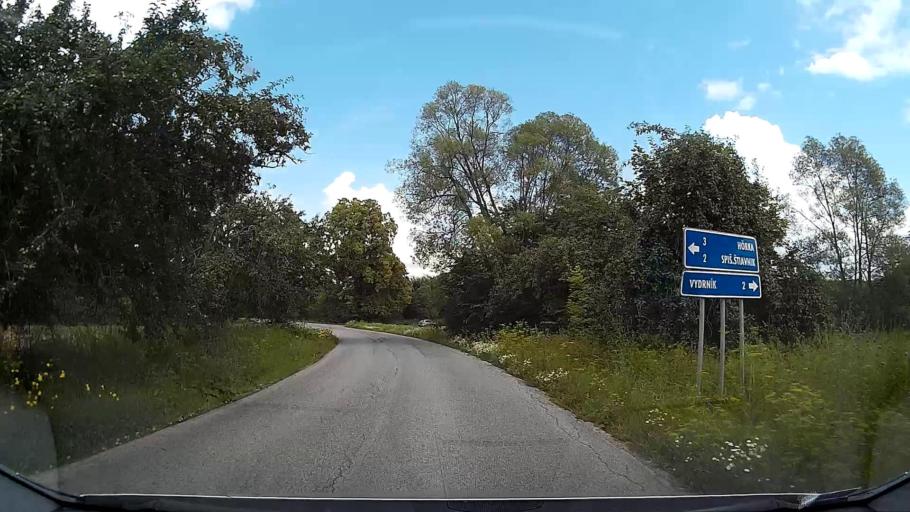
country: SK
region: Presovsky
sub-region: Okres Poprad
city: Poprad
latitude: 48.9901
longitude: 20.3858
